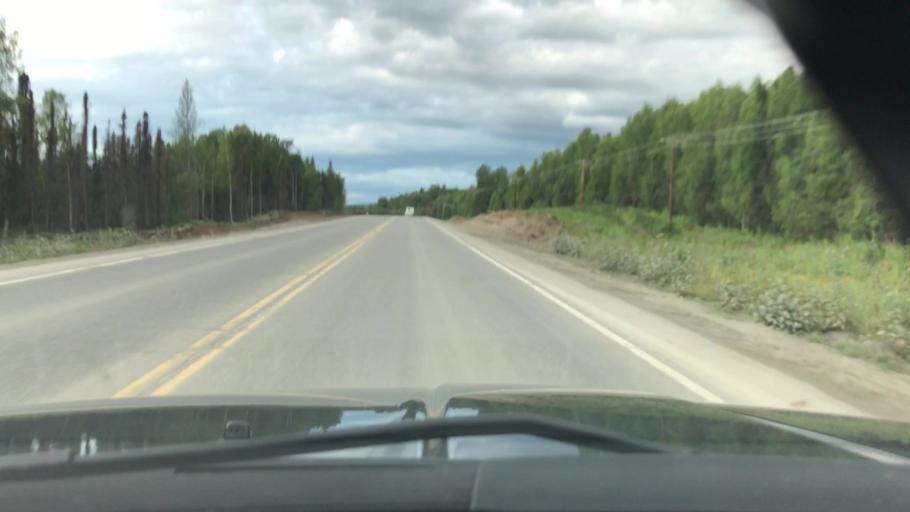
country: US
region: Alaska
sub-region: Matanuska-Susitna Borough
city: Y
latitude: 62.1098
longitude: -150.0570
